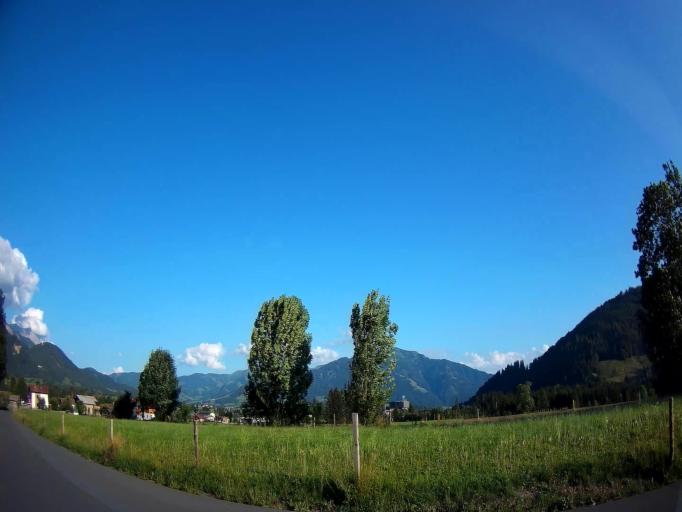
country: AT
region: Salzburg
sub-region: Politischer Bezirk Zell am See
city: Saalfelden am Steinernen Meer
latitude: 47.4509
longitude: 12.8089
